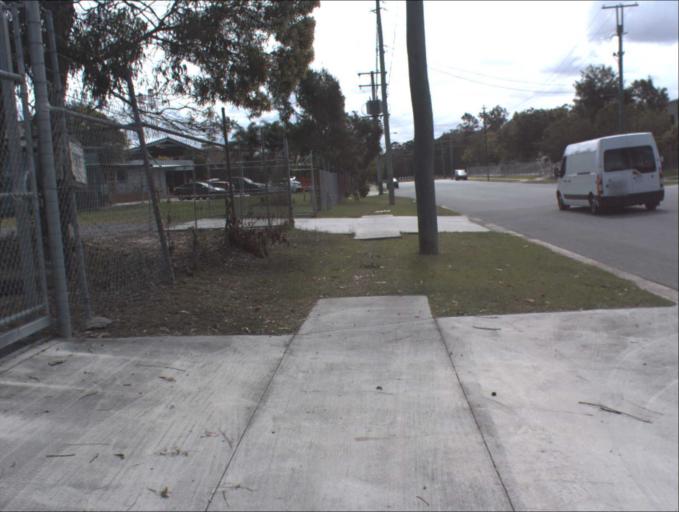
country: AU
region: Queensland
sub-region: Logan
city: Logan Reserve
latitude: -27.6796
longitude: 153.0756
